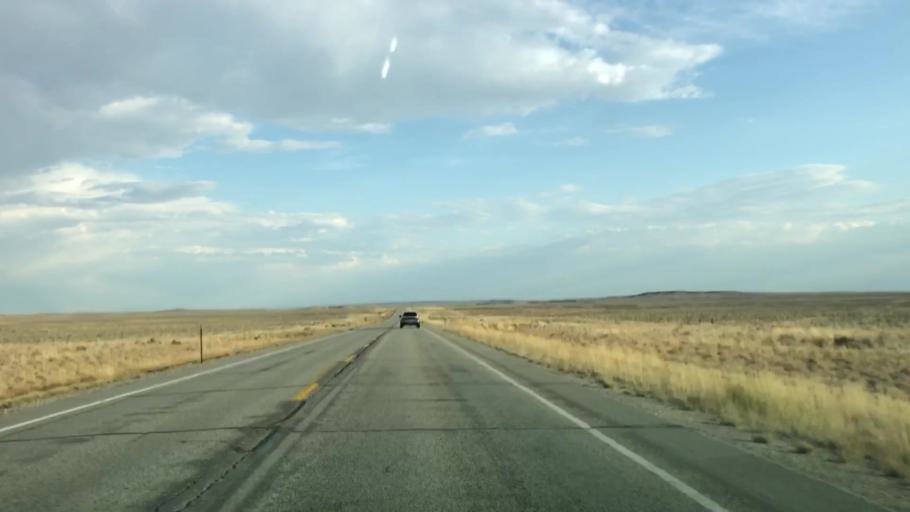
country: US
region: Wyoming
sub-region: Sublette County
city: Pinedale
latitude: 42.3861
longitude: -109.5377
